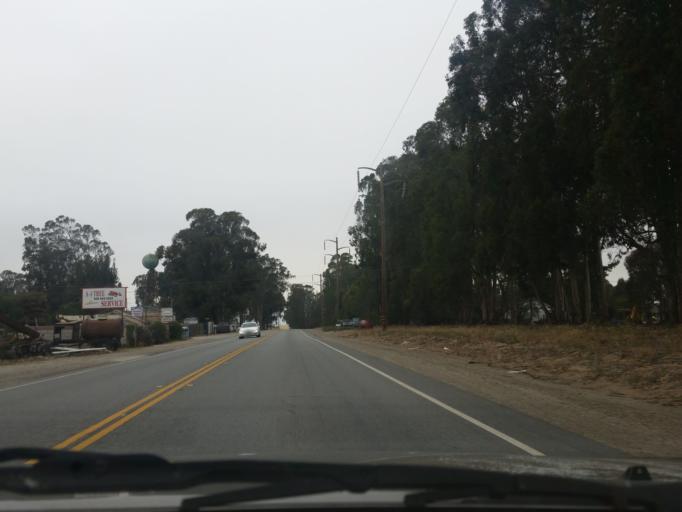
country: US
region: California
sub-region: San Luis Obispo County
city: Callender
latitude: 35.0473
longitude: -120.5815
